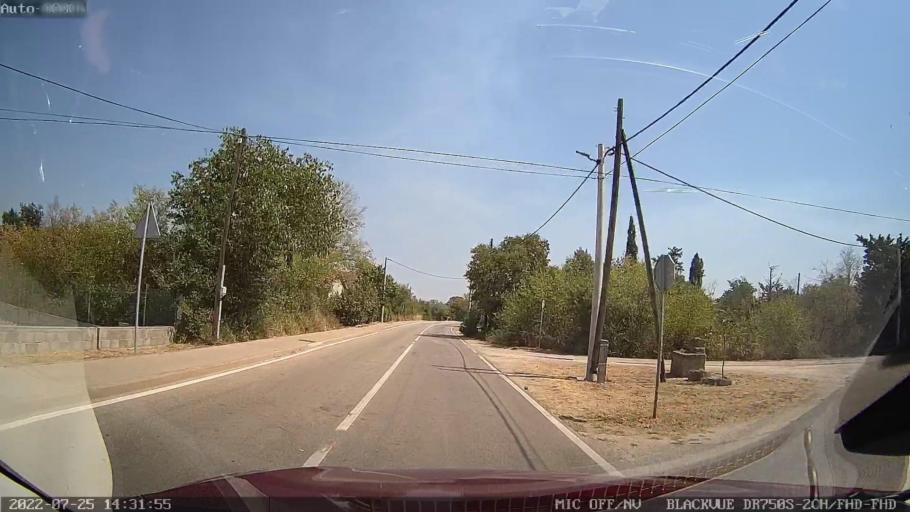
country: HR
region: Zadarska
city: Galovac
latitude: 44.1084
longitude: 15.3760
